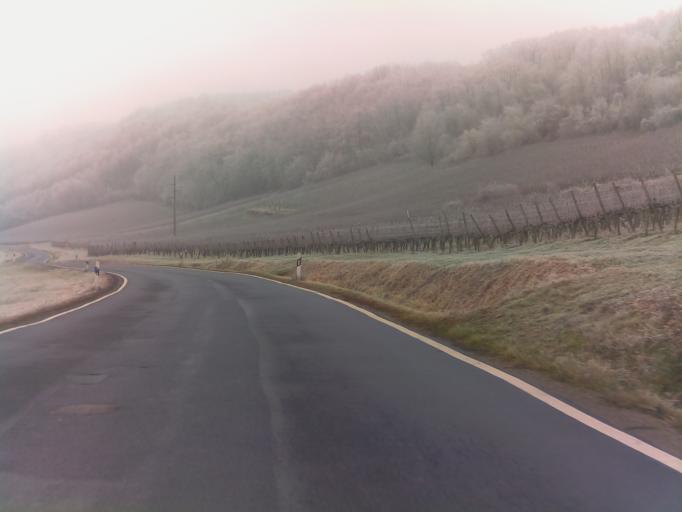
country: DE
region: Bavaria
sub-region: Regierungsbezirk Unterfranken
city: Marktsteft
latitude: 49.6914
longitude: 10.1262
